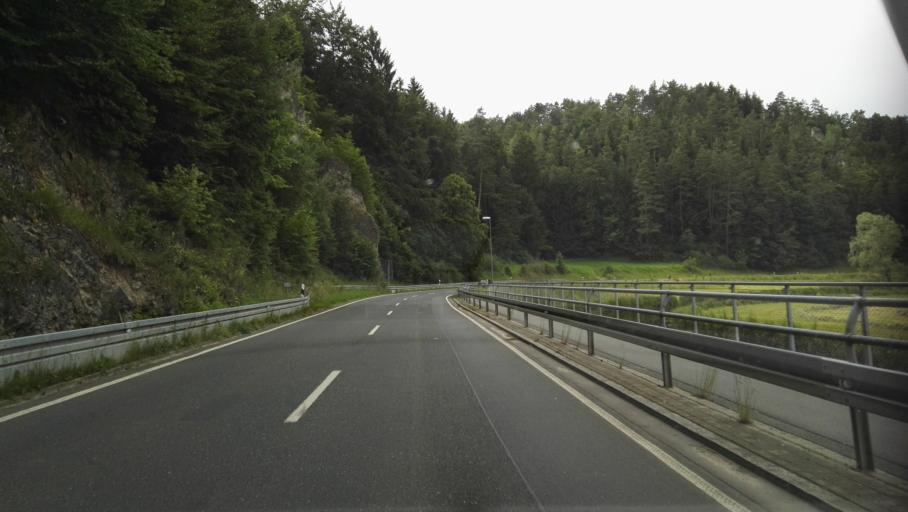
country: DE
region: Bavaria
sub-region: Upper Franconia
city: Waischenfeld
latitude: 49.8536
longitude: 11.3322
